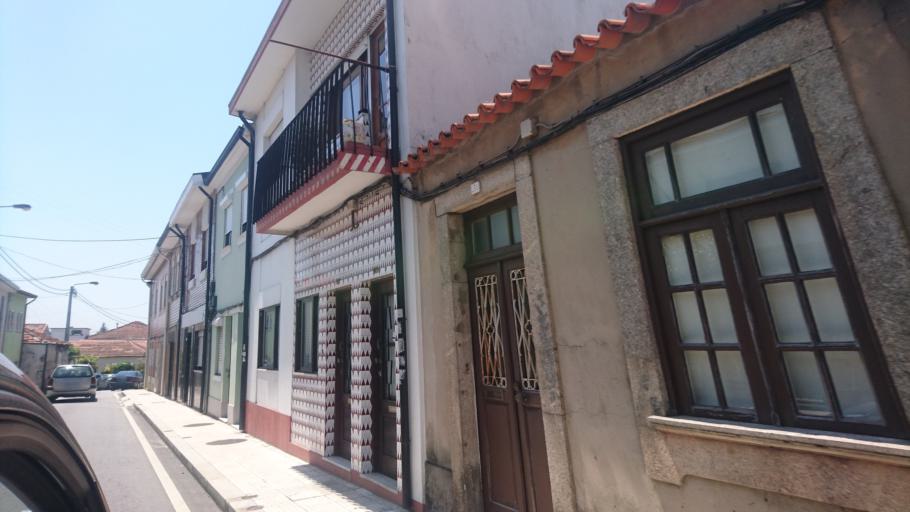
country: PT
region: Porto
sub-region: Gondomar
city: Rio Tinto
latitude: 41.1628
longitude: -8.5474
